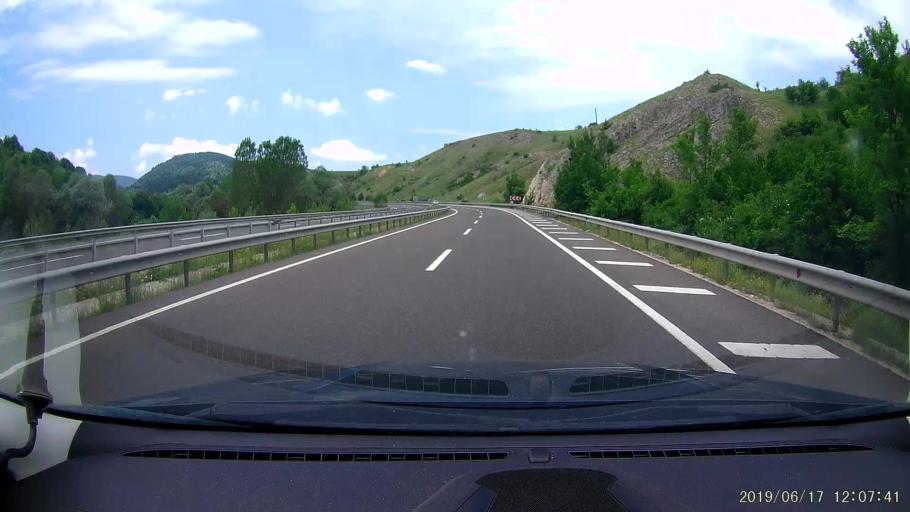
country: TR
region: Cankiri
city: Cerkes
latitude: 40.8349
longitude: 32.7260
